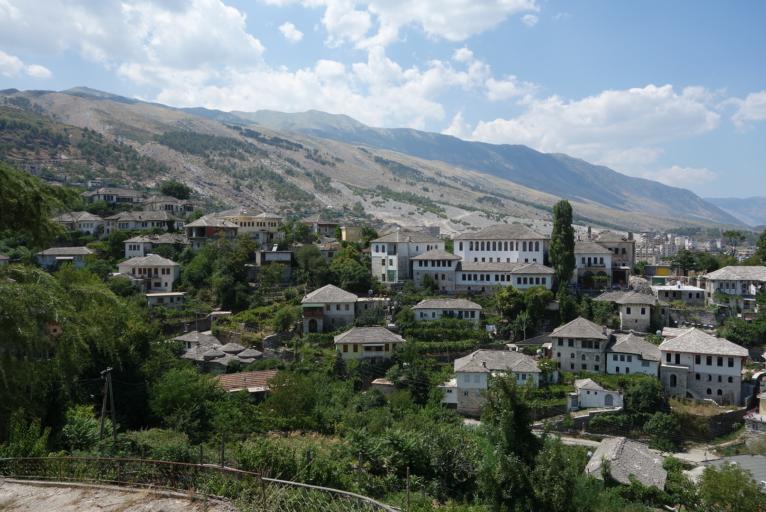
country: AL
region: Gjirokaster
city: Gjirokaster
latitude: 40.0765
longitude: 20.1423
